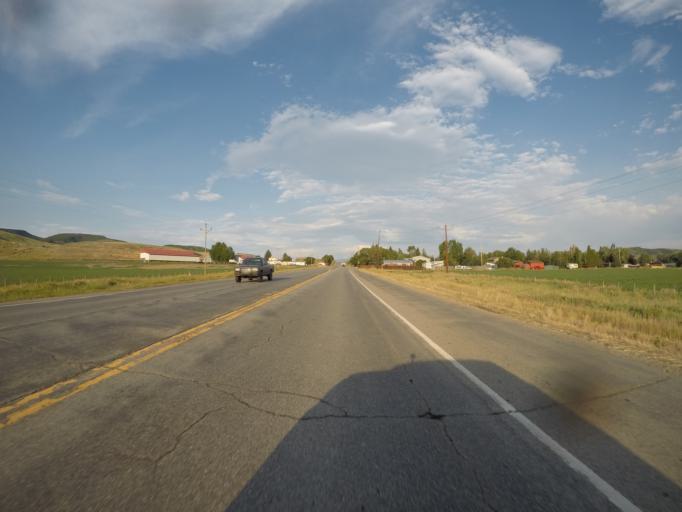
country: US
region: Colorado
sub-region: Routt County
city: Steamboat Springs
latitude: 40.4857
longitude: -107.0247
